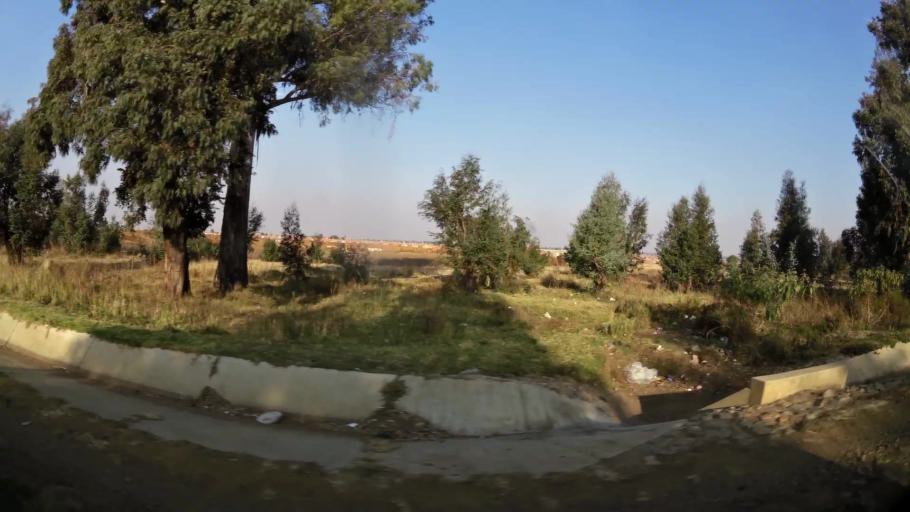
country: ZA
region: Gauteng
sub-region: Ekurhuleni Metropolitan Municipality
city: Benoni
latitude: -26.1488
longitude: 28.3831
